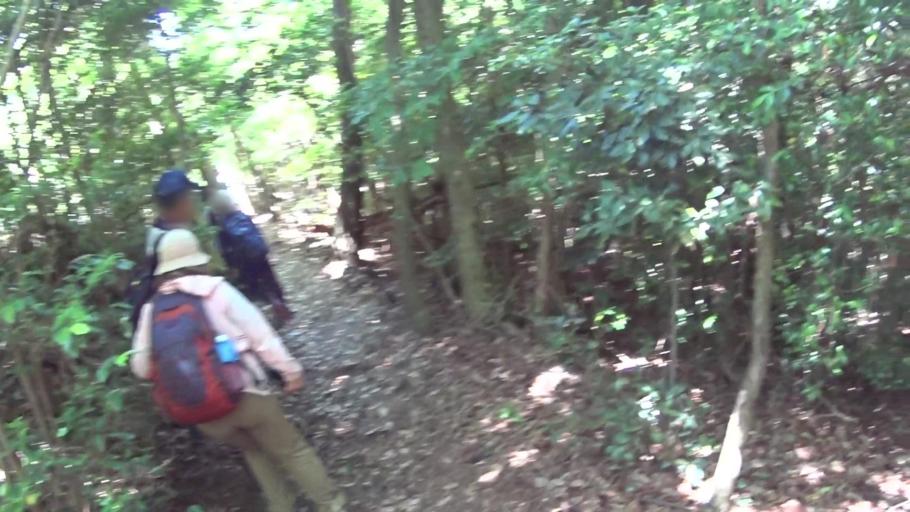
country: JP
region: Kyoto
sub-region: Kyoto-shi
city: Kamigyo-ku
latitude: 35.0460
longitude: 135.8101
